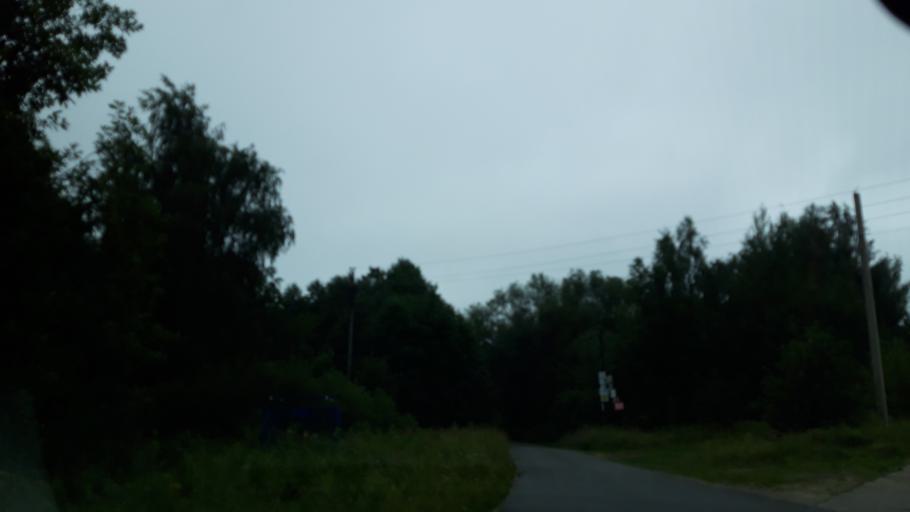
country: RU
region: Tverskaya
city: Konakovo
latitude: 56.6623
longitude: 36.6665
